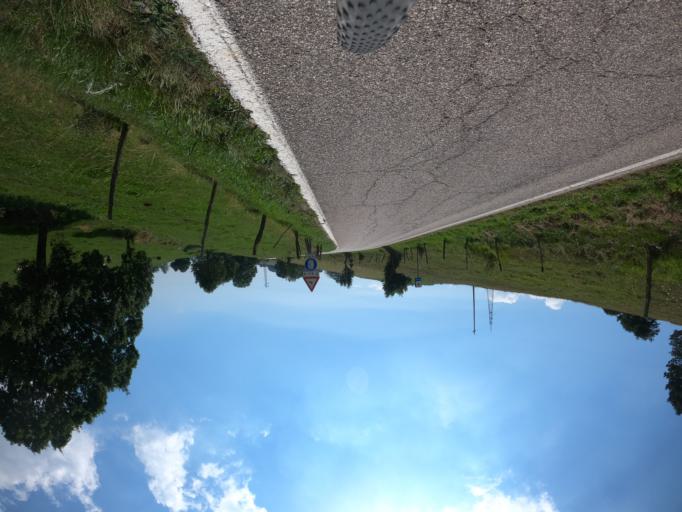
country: IT
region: Veneto
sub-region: Provincia di Verona
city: Ferrara di Monte Baldo
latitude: 45.6656
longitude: 10.8492
